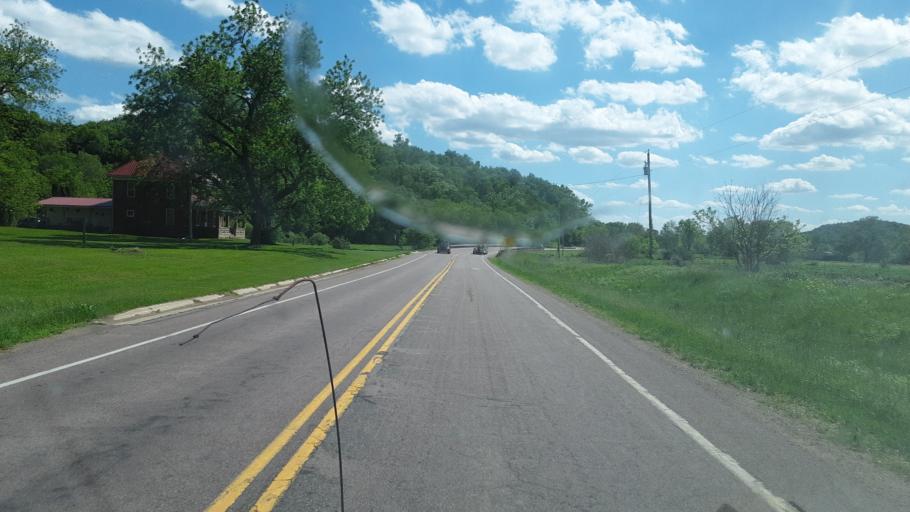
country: US
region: Wisconsin
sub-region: Richland County
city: Richland Center
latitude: 43.3615
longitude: -90.2660
